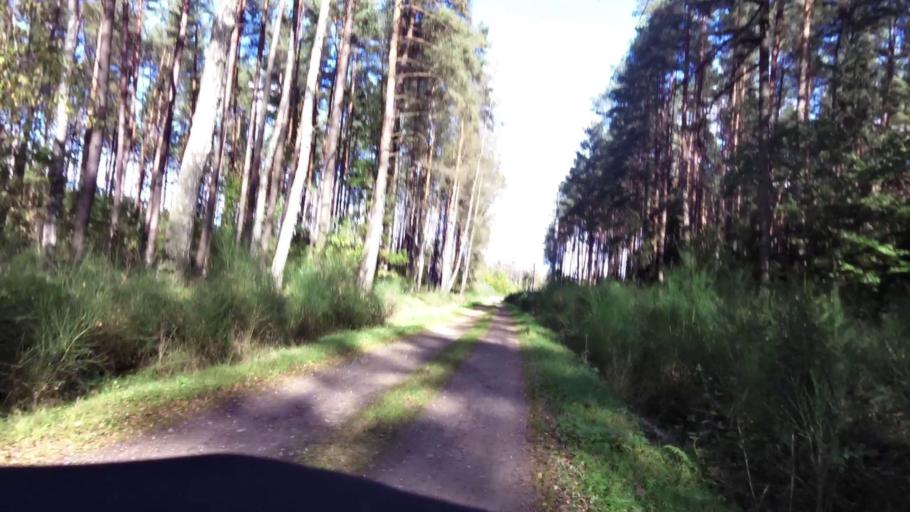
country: PL
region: West Pomeranian Voivodeship
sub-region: Powiat bialogardzki
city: Tychowo
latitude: 54.0289
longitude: 16.1524
